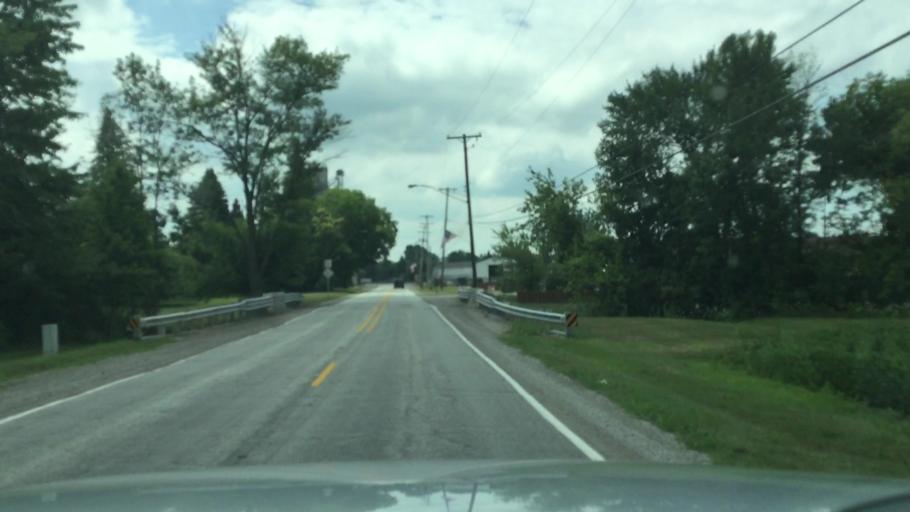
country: US
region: Michigan
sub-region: Saginaw County
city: Birch Run
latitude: 43.2541
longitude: -83.7943
